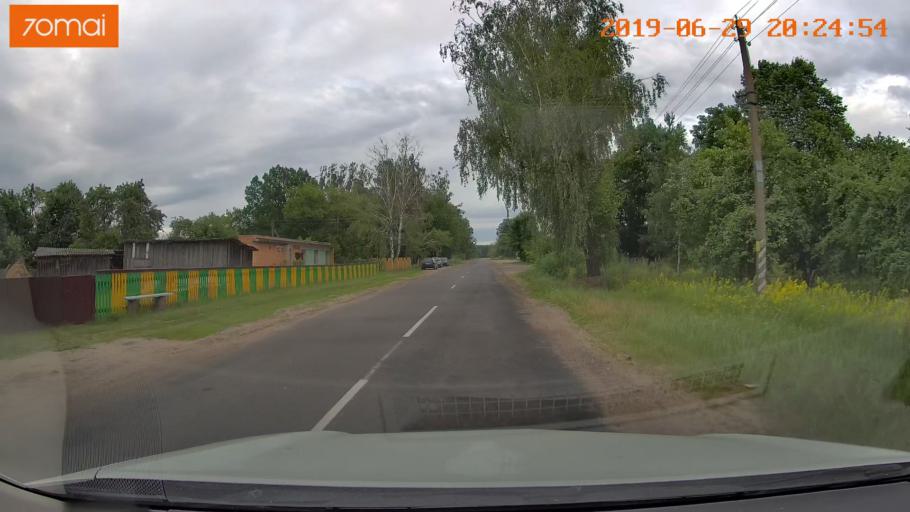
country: BY
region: Brest
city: Asnyezhytsy
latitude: 52.4553
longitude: 26.2729
